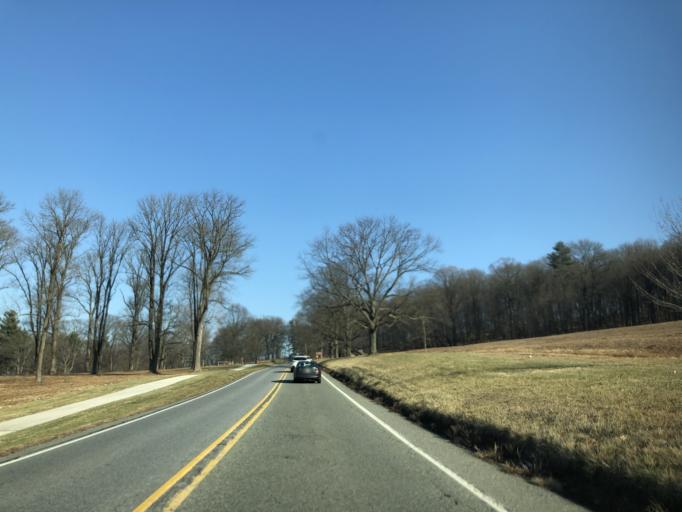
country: US
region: Pennsylvania
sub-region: Chester County
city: Chesterbrook
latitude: 40.1012
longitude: -75.4566
